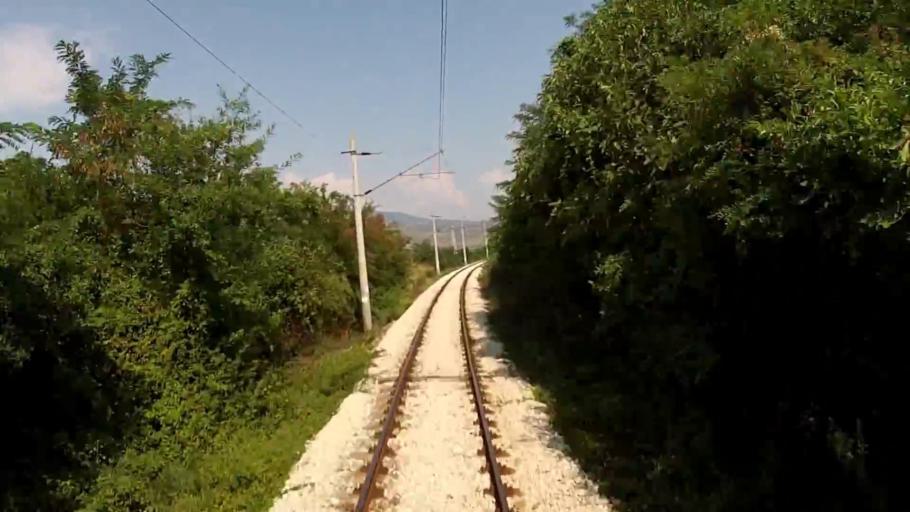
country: BG
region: Blagoevgrad
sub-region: Obshtina Sandanski
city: Sandanski
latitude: 41.5298
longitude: 23.2597
